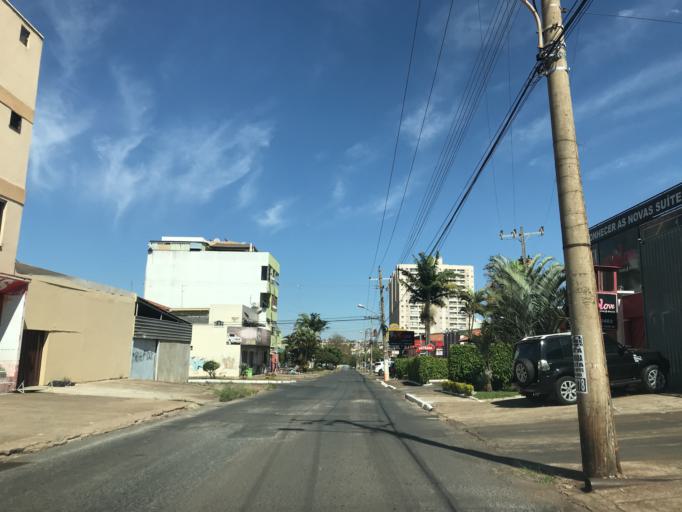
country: BR
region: Federal District
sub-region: Brasilia
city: Brasilia
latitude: -15.8113
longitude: -48.0700
